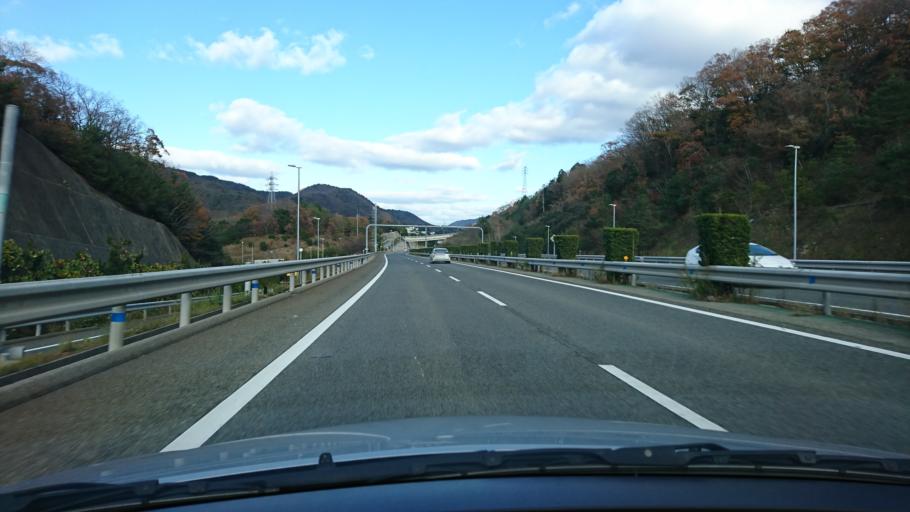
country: JP
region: Hyogo
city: Kobe
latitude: 34.7564
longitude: 135.1566
